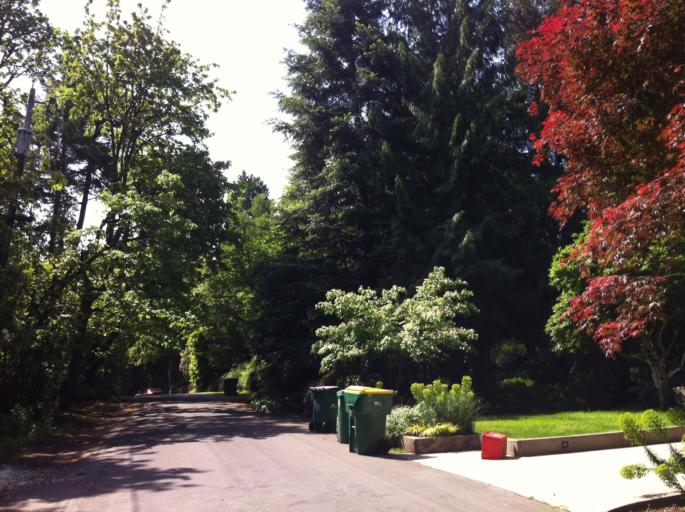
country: US
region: Oregon
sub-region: Washington County
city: Raleigh Hills
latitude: 45.4905
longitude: -122.7501
